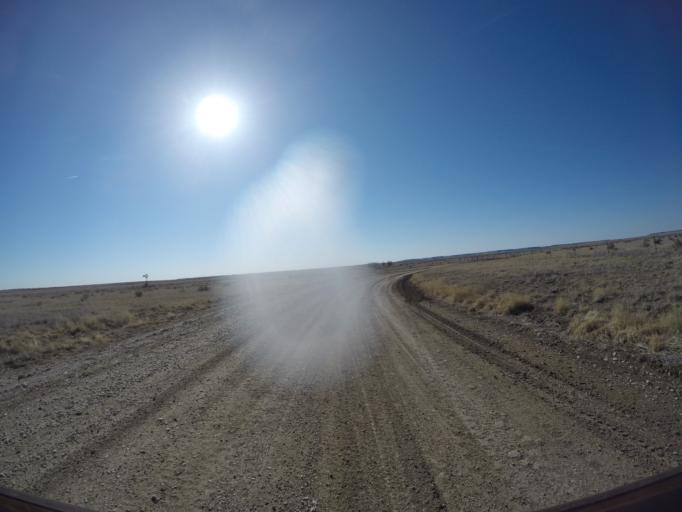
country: US
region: Colorado
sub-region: Otero County
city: La Junta
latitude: 37.6893
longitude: -103.6204
